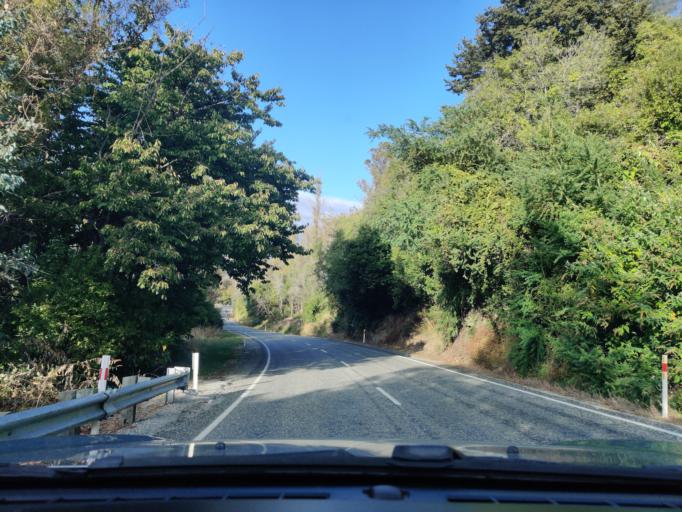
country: NZ
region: Otago
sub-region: Queenstown-Lakes District
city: Queenstown
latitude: -45.0427
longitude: 168.6348
